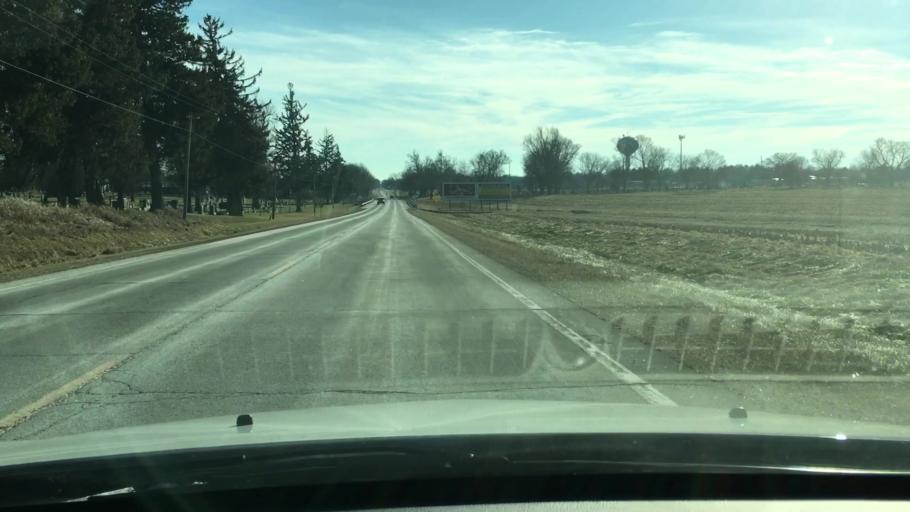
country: US
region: Illinois
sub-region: LaSalle County
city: Mendota
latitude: 41.5676
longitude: -89.1281
